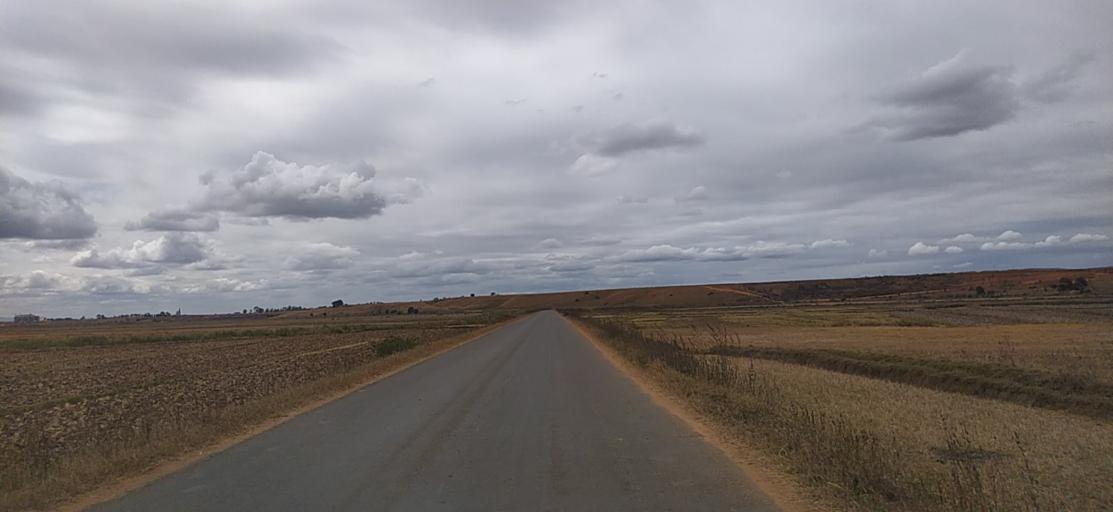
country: MG
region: Alaotra Mangoro
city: Ambatondrazaka
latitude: -17.9189
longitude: 48.2580
